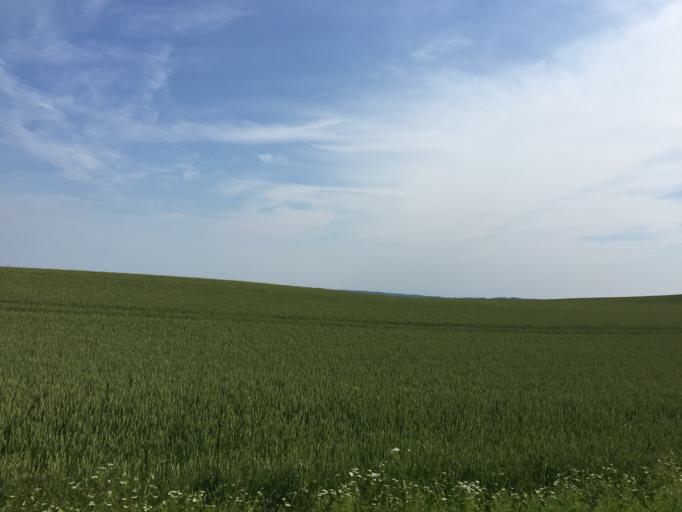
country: DK
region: South Denmark
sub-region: Kerteminde Kommune
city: Kerteminde
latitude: 55.4704
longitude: 10.6902
